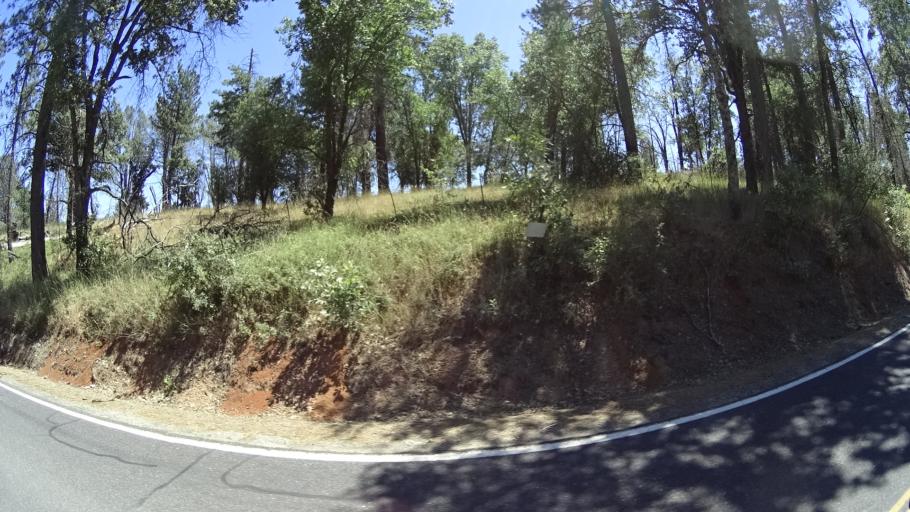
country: US
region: California
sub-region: Calaveras County
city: Mountain Ranch
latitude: 38.3096
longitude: -120.5096
